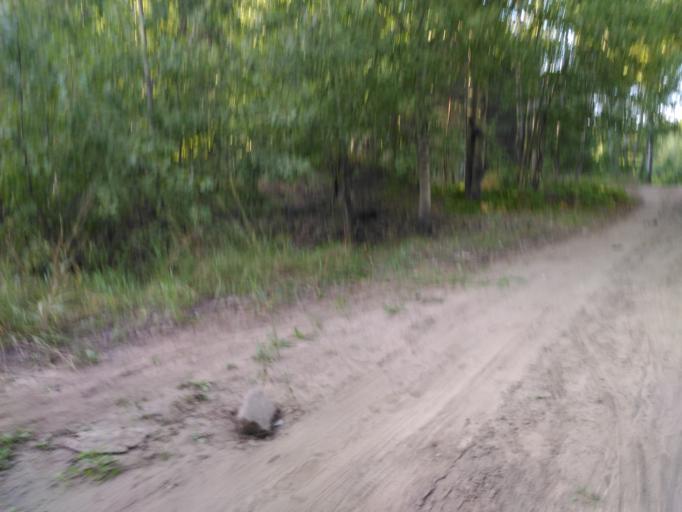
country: RU
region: Ulyanovsk
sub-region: Ulyanovskiy Rayon
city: Ulyanovsk
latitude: 54.3560
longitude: 48.5170
